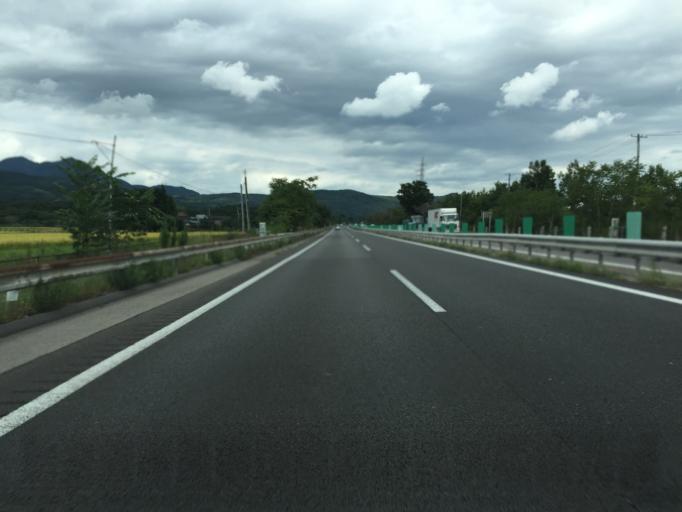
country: JP
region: Miyagi
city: Shiroishi
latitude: 38.0233
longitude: 140.6236
